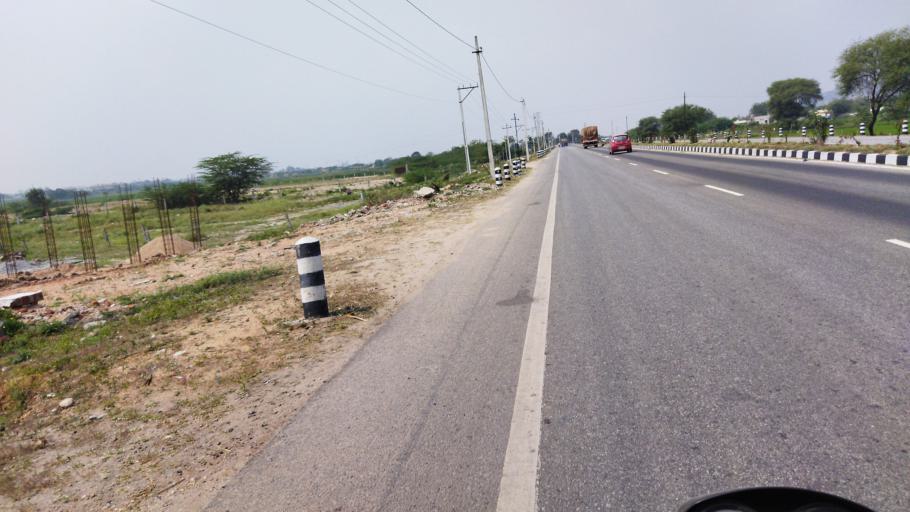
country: IN
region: Telangana
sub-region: Nalgonda
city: Nalgonda
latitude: 17.0769
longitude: 79.2816
